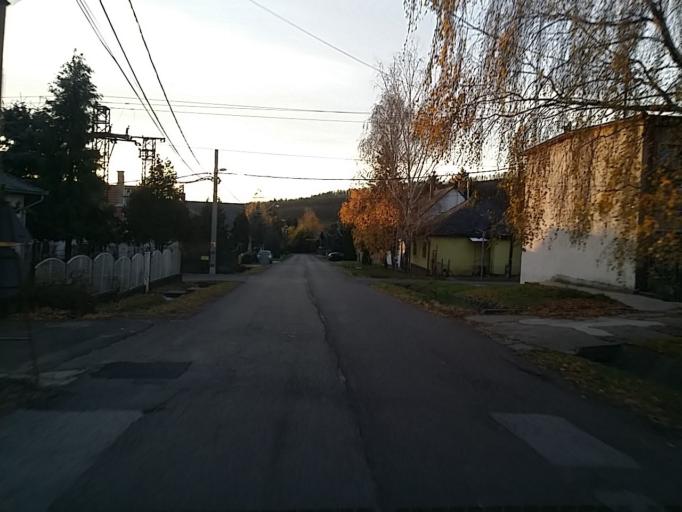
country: HU
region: Heves
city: Gyongyossolymos
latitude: 47.8252
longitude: 19.9729
